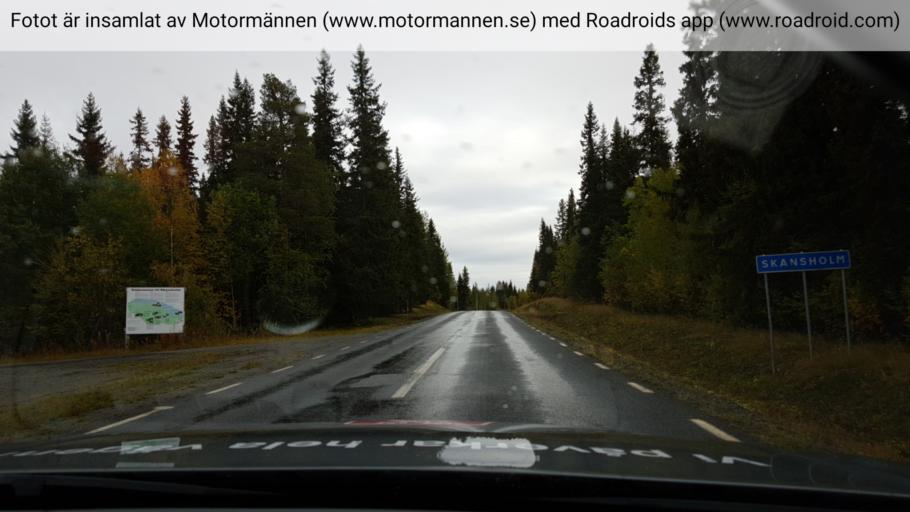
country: SE
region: Vaesterbotten
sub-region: Vilhelmina Kommun
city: Sjoberg
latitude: 64.7023
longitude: 16.2588
